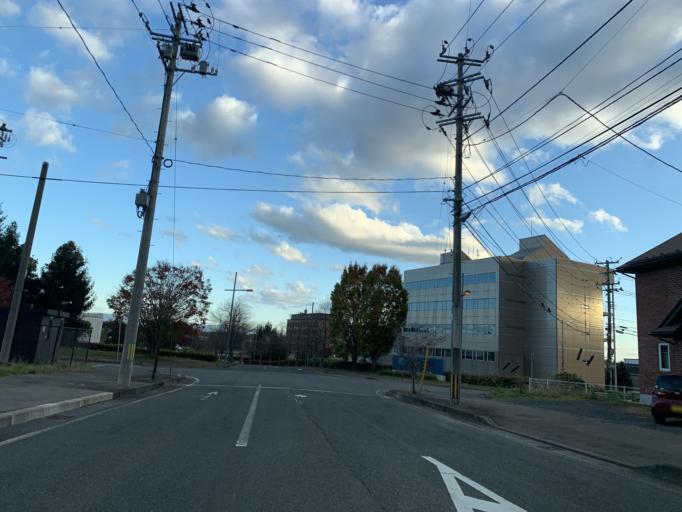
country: JP
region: Iwate
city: Kitakami
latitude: 39.2584
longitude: 141.1054
